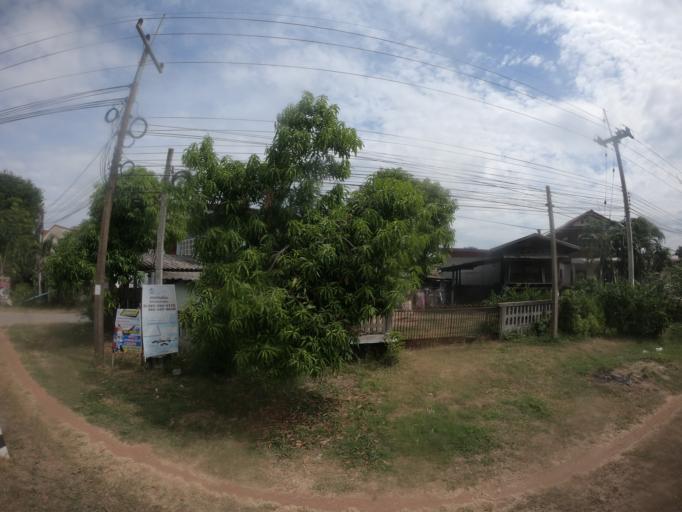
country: TH
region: Maha Sarakham
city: Chiang Yuen
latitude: 16.3667
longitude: 103.1059
